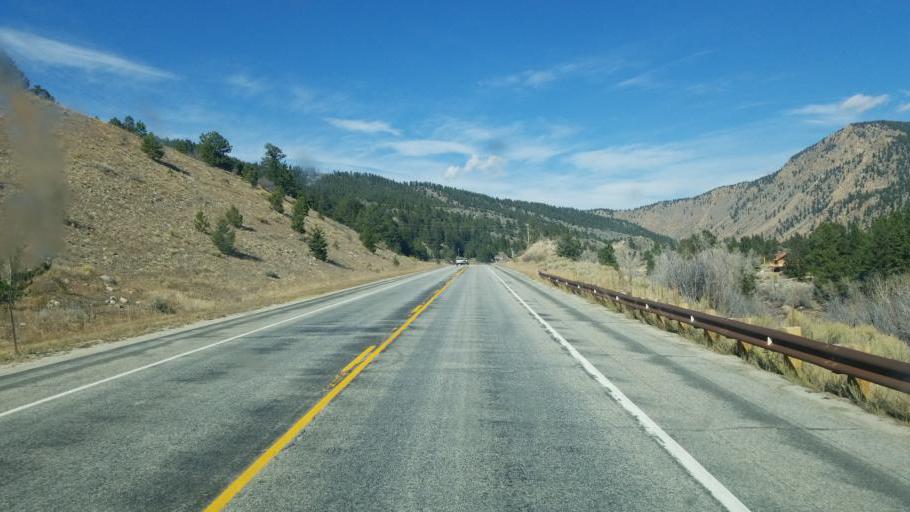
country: US
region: Colorado
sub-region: Chaffee County
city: Buena Vista
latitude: 38.9733
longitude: -106.2119
